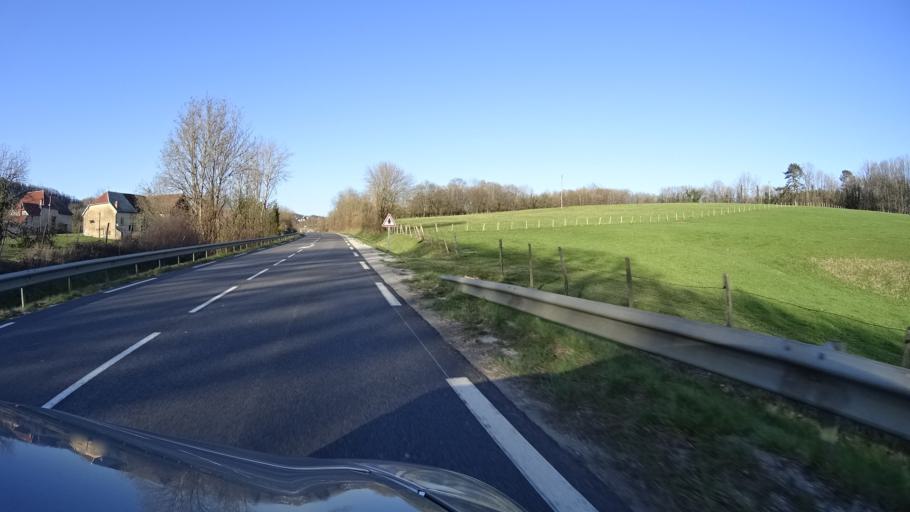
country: FR
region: Franche-Comte
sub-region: Departement du Doubs
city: Beure
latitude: 47.1875
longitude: 6.0127
